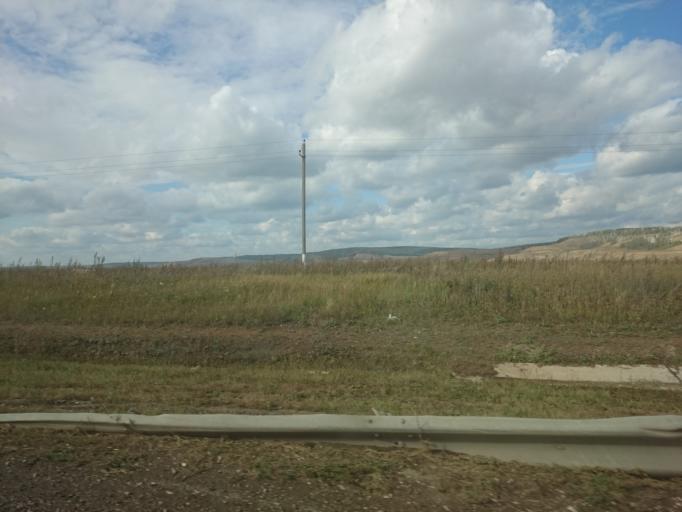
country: RU
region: Samara
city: Kamyshla
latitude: 54.0716
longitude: 52.1978
